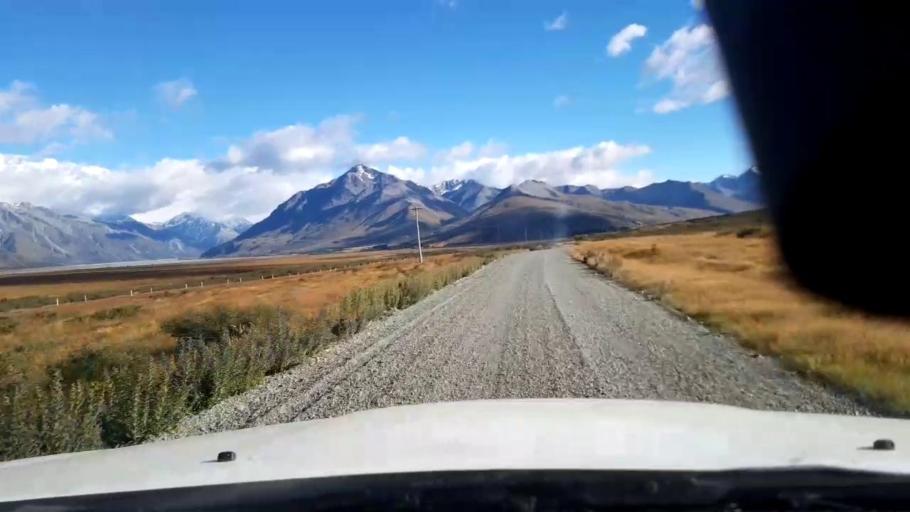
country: NZ
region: Canterbury
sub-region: Timaru District
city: Pleasant Point
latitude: -43.7581
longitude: 170.5698
